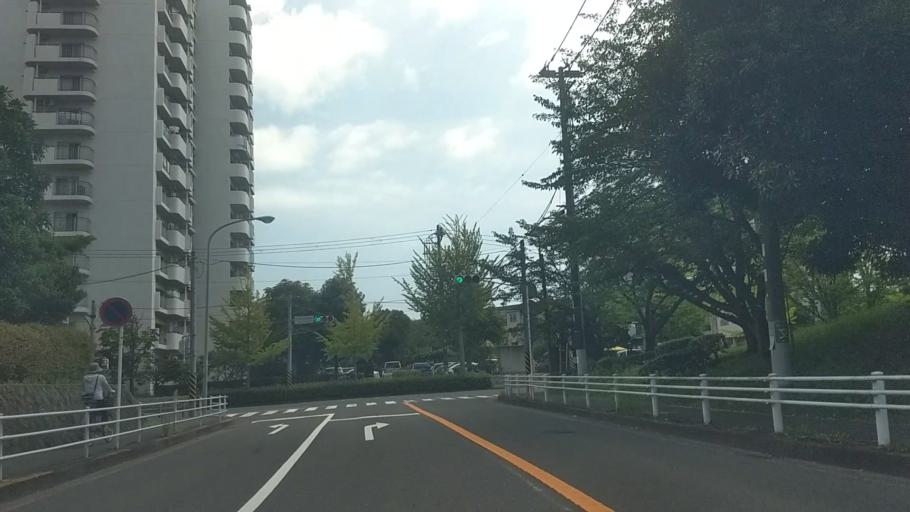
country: JP
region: Kanagawa
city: Yokosuka
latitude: 35.3567
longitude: 139.6384
